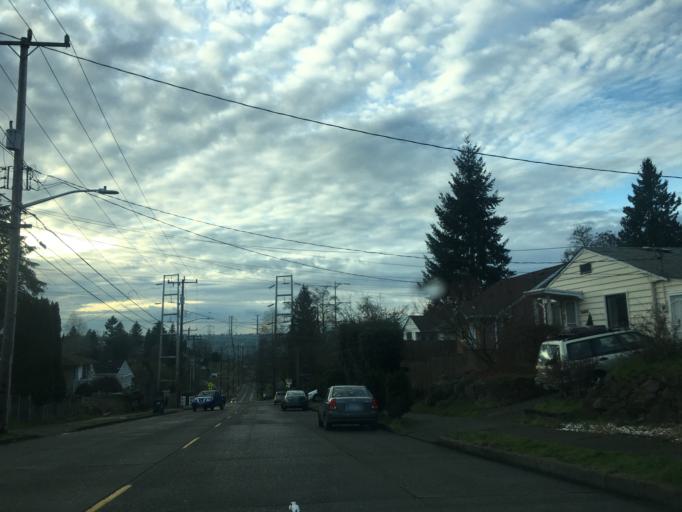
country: US
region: Washington
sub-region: King County
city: Bryn Mawr-Skyway
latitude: 47.5062
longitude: -122.2635
